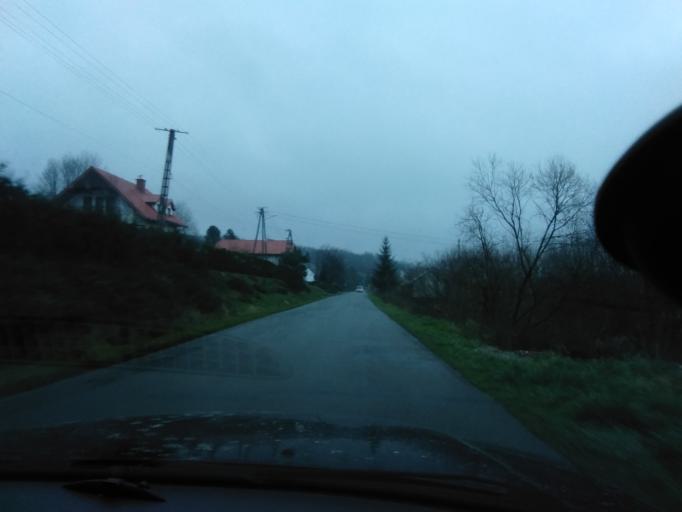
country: PL
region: Subcarpathian Voivodeship
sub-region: Powiat brzozowski
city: Jablonka
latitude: 49.7451
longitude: 22.1261
